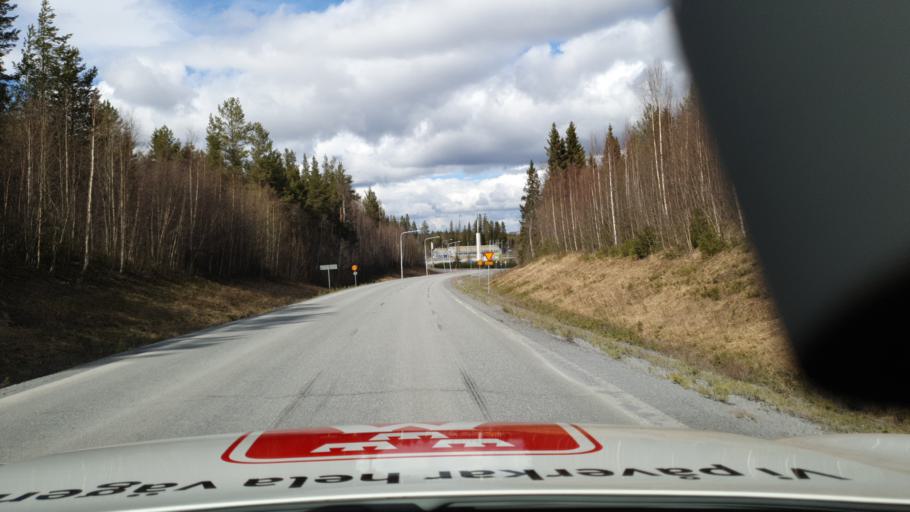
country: SE
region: Jaemtland
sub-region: Krokoms Kommun
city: Krokom
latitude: 63.3258
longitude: 14.4267
